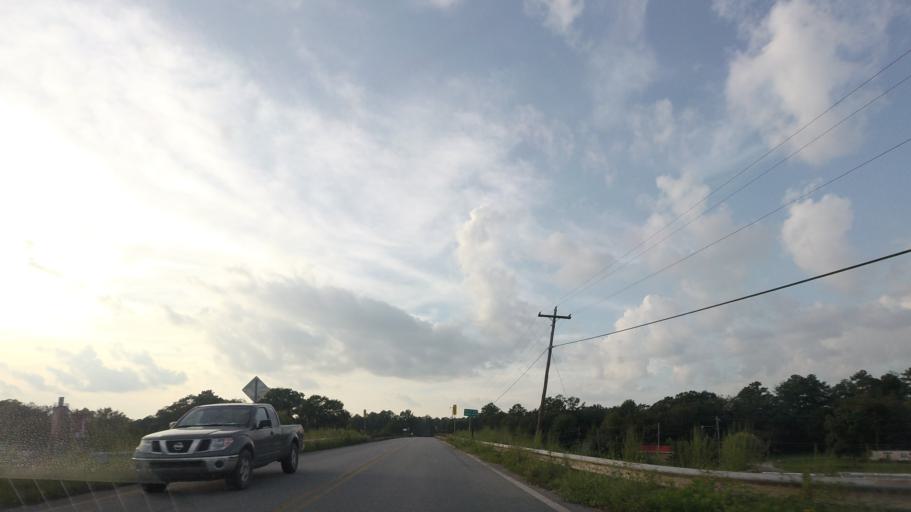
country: US
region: Georgia
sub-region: Wilkinson County
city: Gordon
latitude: 32.8820
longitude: -83.3421
